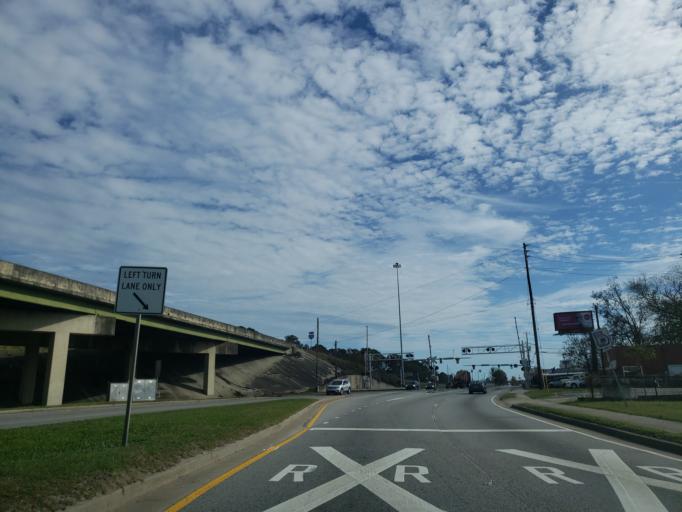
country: US
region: Georgia
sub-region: Chatham County
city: Garden City
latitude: 32.0975
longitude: -81.1403
